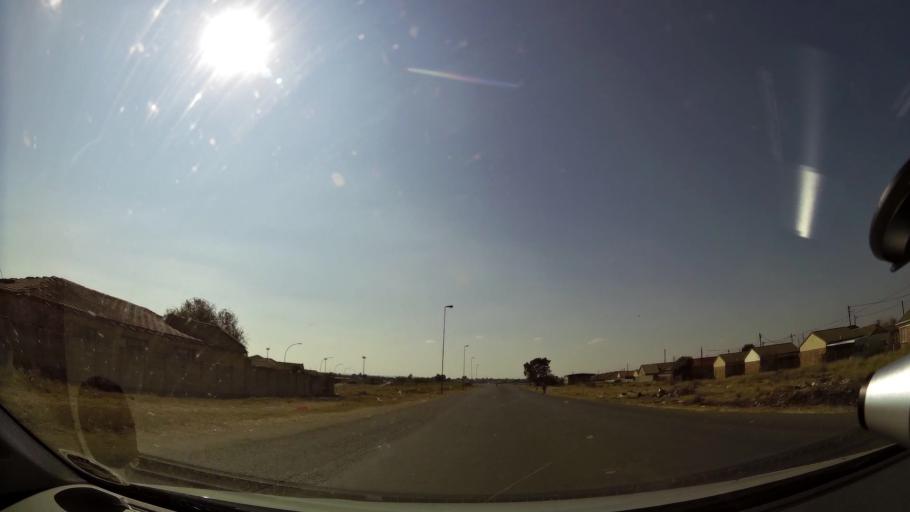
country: ZA
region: Orange Free State
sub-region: Mangaung Metropolitan Municipality
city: Bloemfontein
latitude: -29.1529
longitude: 26.2593
